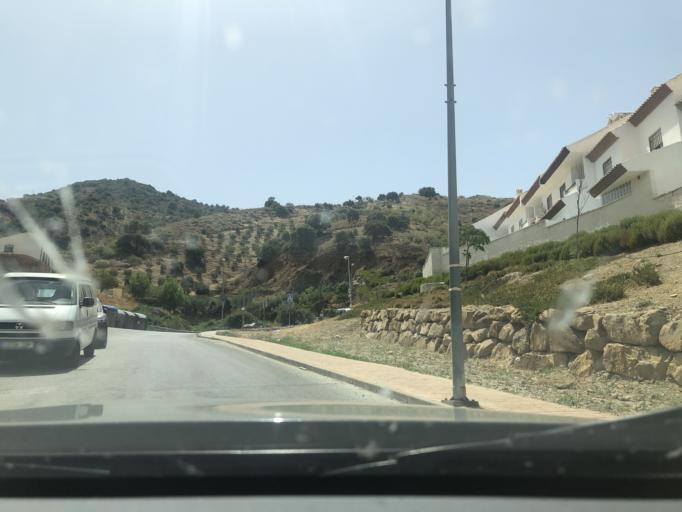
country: ES
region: Andalusia
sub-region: Provincia de Malaga
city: Cartama
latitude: 36.7115
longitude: -4.6253
